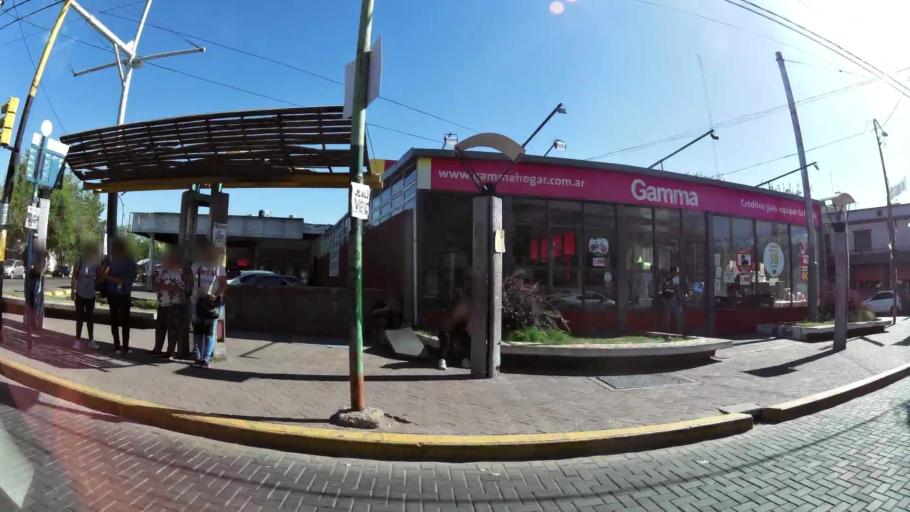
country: AR
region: Mendoza
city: Villa Nueva
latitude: -32.9036
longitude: -68.7889
